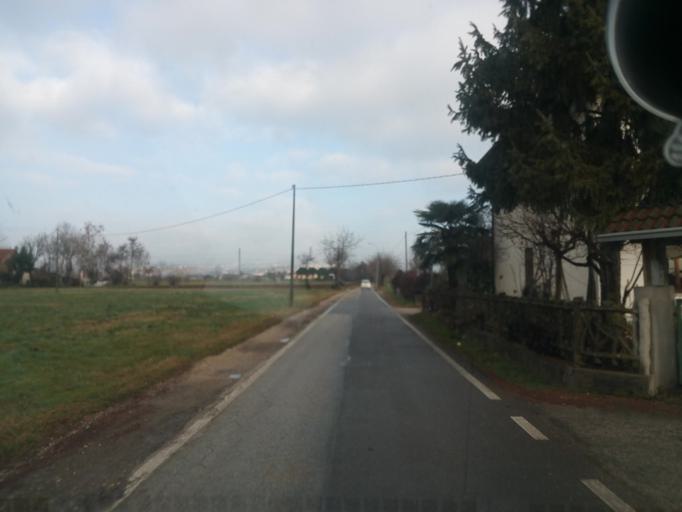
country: IT
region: Veneto
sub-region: Provincia di Vicenza
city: Sandrigo
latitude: 45.6717
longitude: 11.5812
